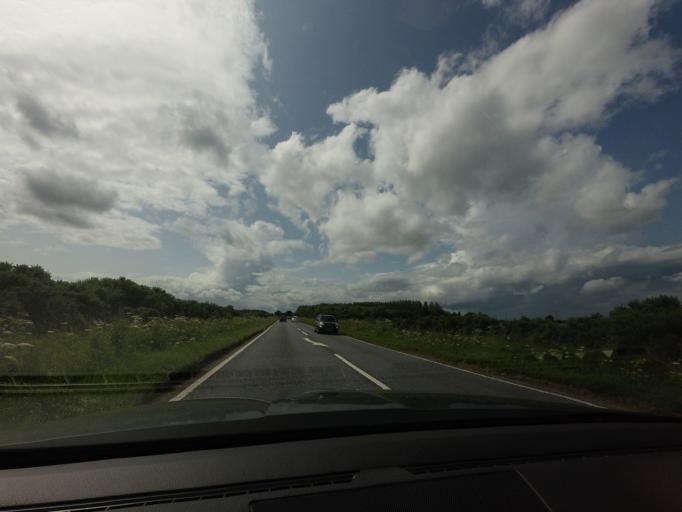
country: GB
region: Scotland
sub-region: Moray
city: Forres
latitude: 57.5854
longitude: -3.7446
